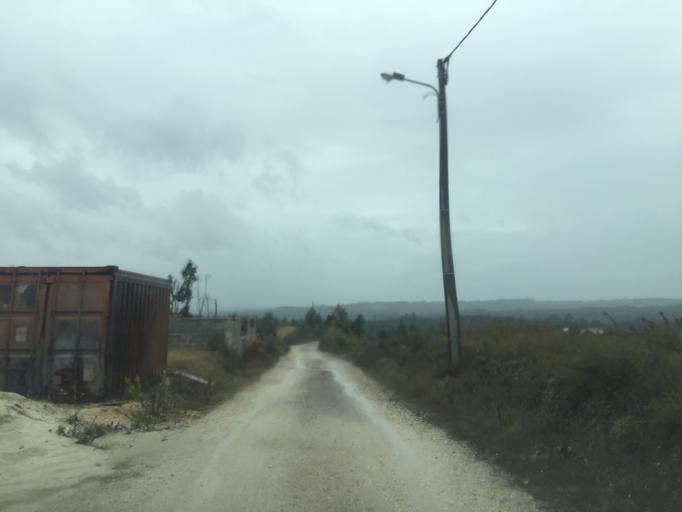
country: PT
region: Coimbra
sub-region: Figueira da Foz
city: Lavos
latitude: 40.0770
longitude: -8.7885
